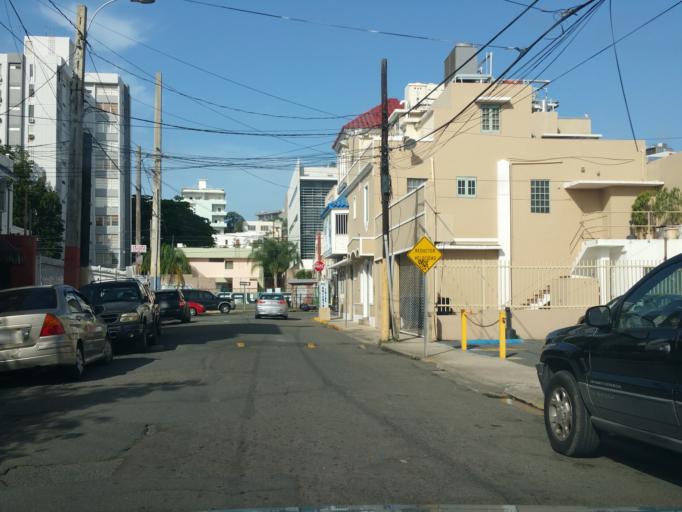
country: PR
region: San Juan
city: San Juan
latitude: 18.4450
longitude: -66.0716
